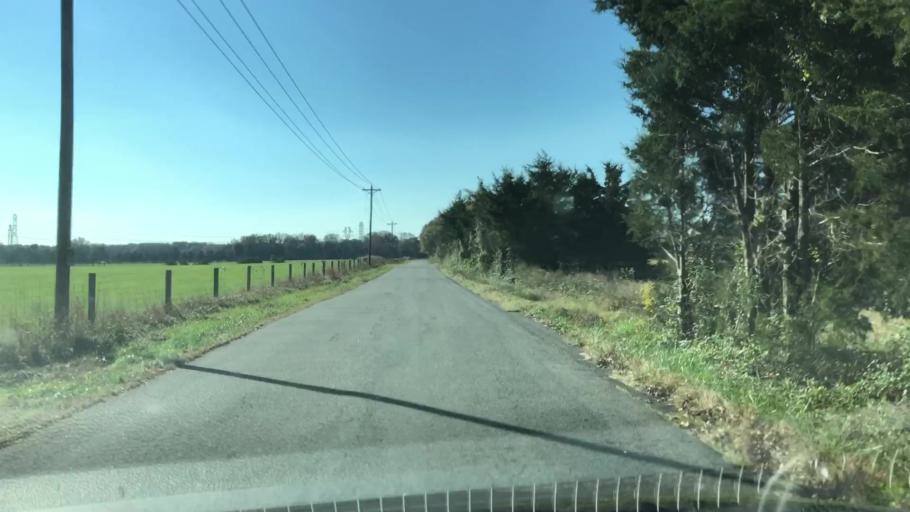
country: US
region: Virginia
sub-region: Fauquier County
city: Bealeton
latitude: 38.5212
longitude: -77.7395
